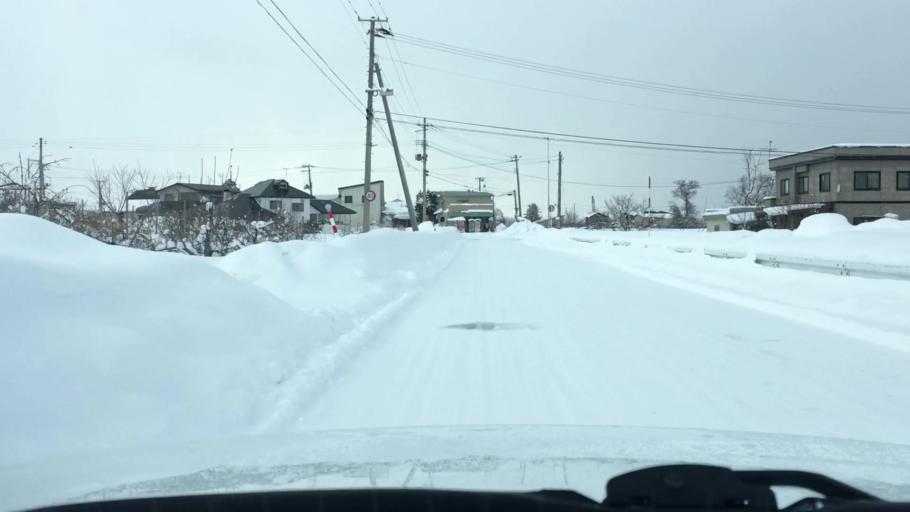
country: JP
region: Aomori
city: Hirosaki
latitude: 40.6548
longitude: 140.4788
